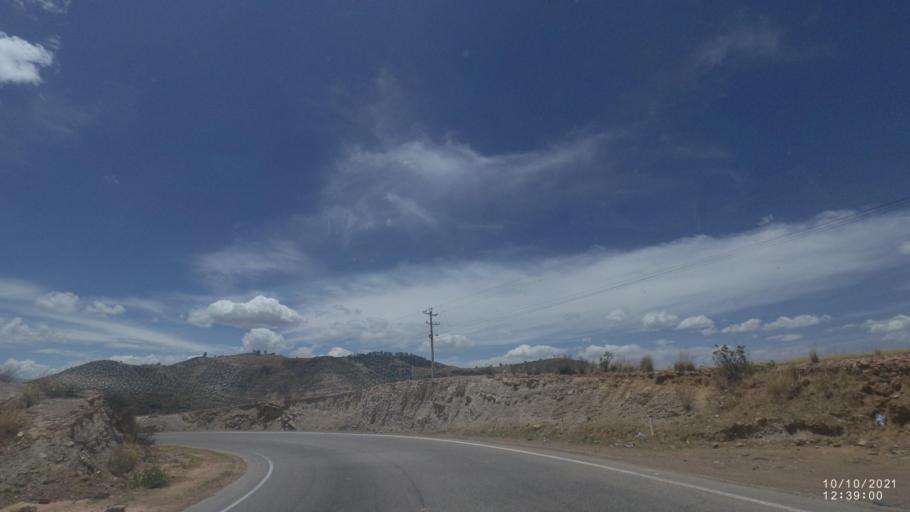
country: BO
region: Cochabamba
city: Irpa Irpa
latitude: -17.6481
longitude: -66.3928
